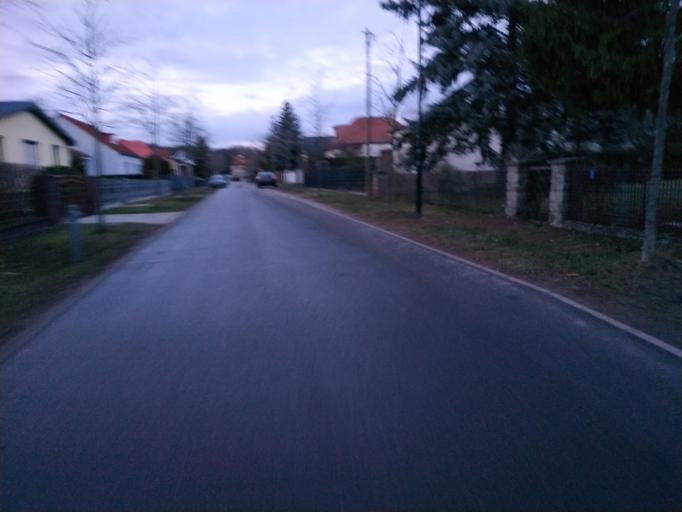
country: DE
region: Brandenburg
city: Petershagen
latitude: 52.5374
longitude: 13.8191
